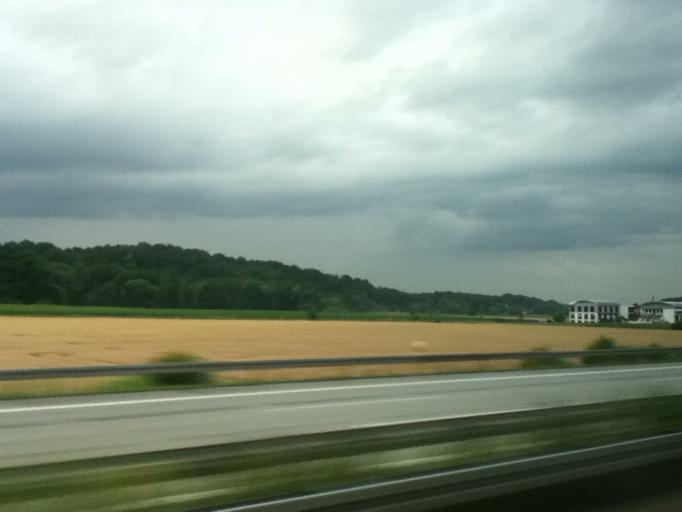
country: DE
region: Saxony
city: Remse
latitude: 50.8436
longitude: 12.5461
